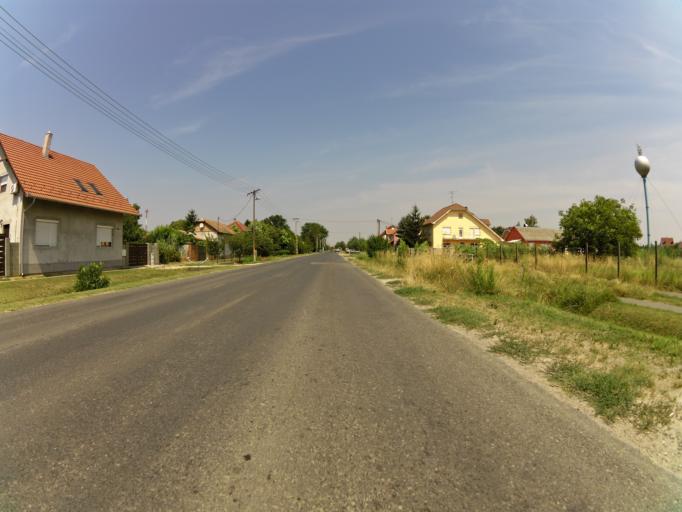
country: HU
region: Csongrad
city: Sandorfalva
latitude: 46.3641
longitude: 20.1008
